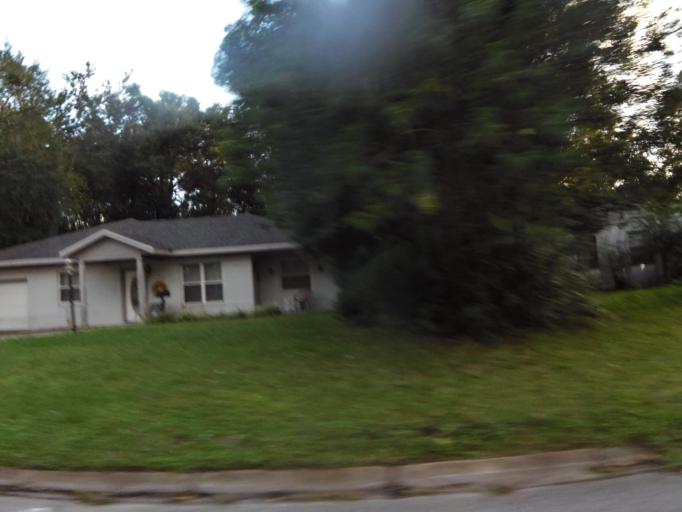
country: US
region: Florida
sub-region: Duval County
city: Jacksonville
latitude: 30.2925
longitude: -81.6304
